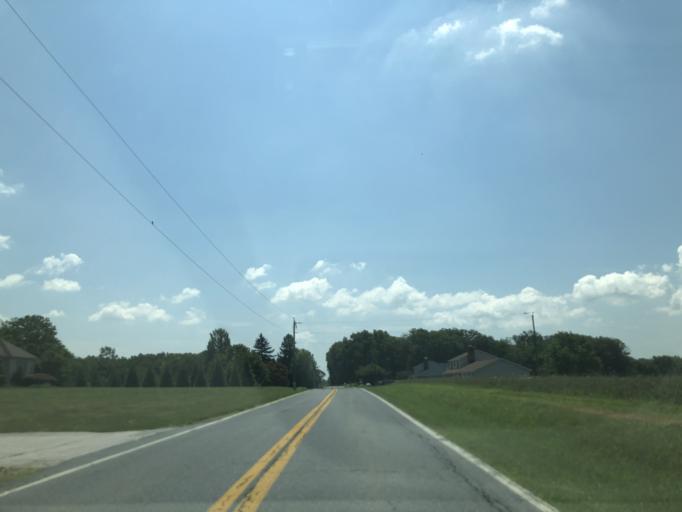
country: US
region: Maryland
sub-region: Carroll County
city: Westminster
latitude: 39.5314
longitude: -76.9614
